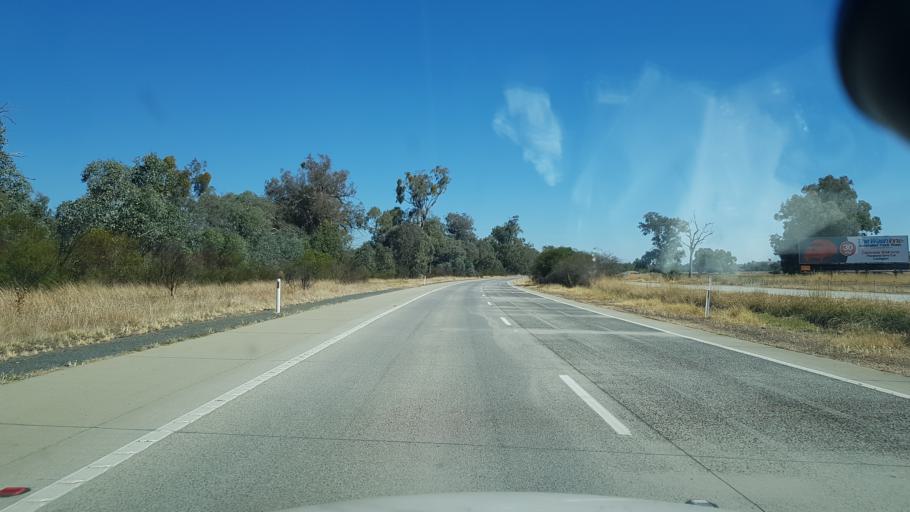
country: AU
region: New South Wales
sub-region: Greater Hume Shire
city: Holbrook
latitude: -35.9022
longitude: 147.1646
